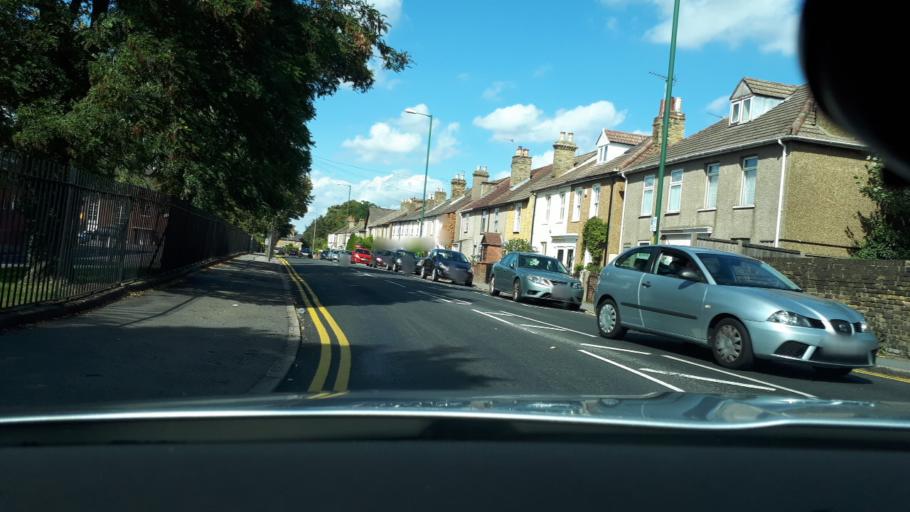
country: GB
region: England
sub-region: Kent
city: Dartford
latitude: 51.4440
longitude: 0.2058
